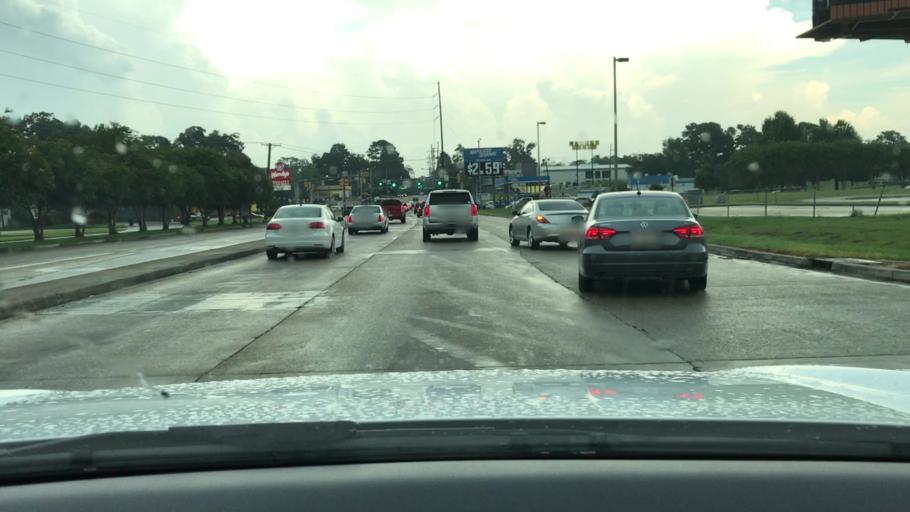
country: US
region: Louisiana
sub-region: East Baton Rouge Parish
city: Baton Rouge
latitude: 30.4247
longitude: -91.1383
